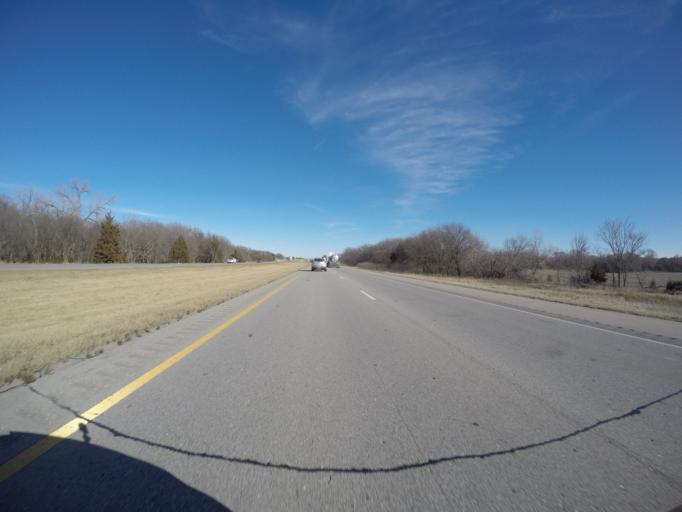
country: US
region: Nebraska
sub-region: Seward County
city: Milford
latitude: 40.8204
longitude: -96.8664
